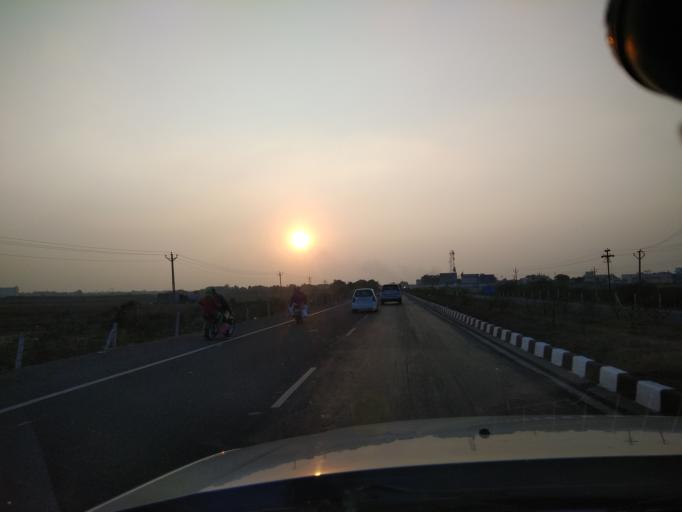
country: IN
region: Gujarat
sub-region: Jamnagar
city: Jamnagar
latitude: 22.4513
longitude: 70.0158
